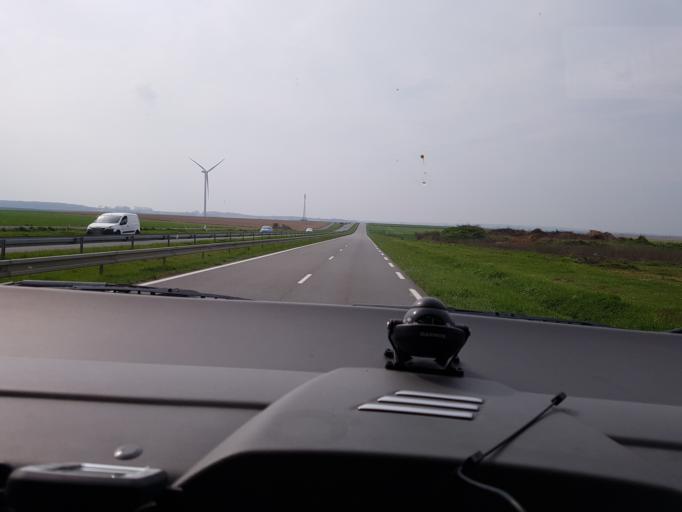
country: FR
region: Picardie
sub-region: Departement de l'Aisne
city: Essigny-le-Grand
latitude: 49.7727
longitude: 3.2821
